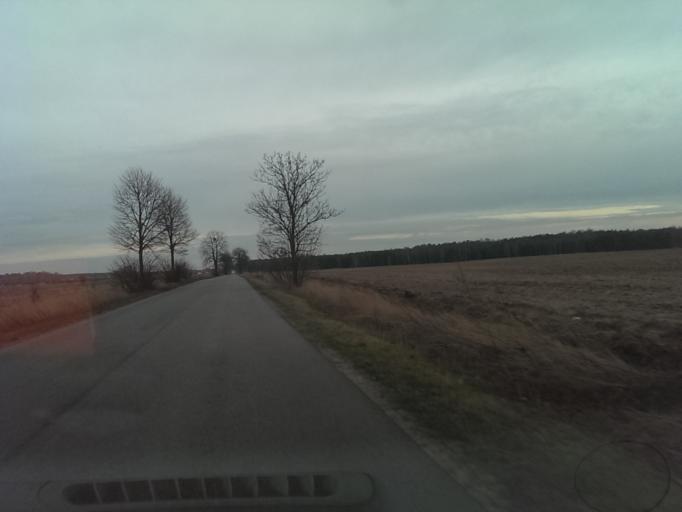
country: PL
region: Kujawsko-Pomorskie
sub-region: Powiat nakielski
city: Szubin
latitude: 53.0826
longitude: 17.7766
